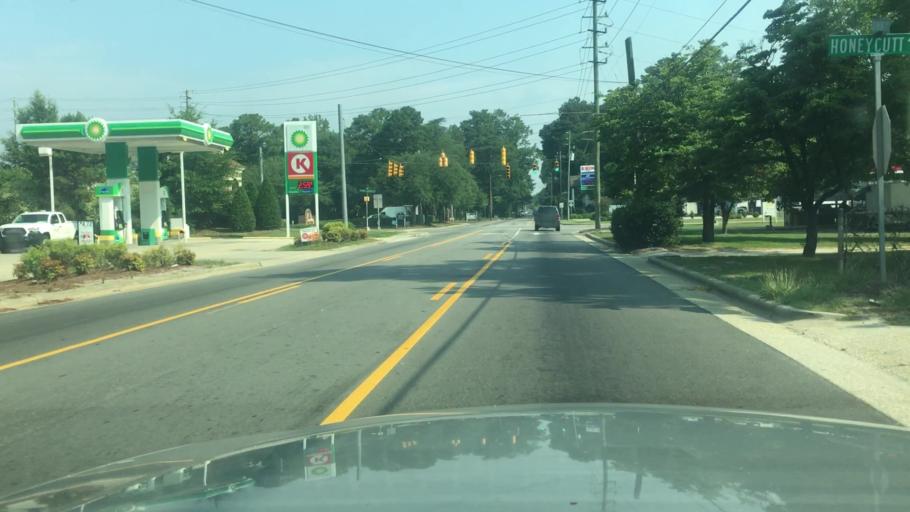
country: US
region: North Carolina
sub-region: Cumberland County
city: Hope Mills
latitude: 34.9651
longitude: -78.9438
